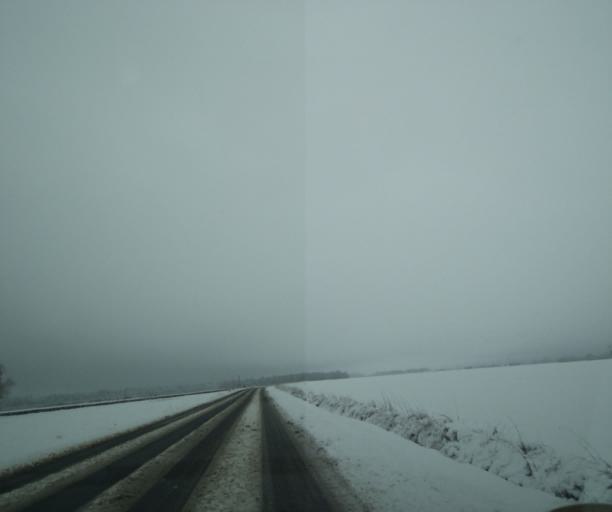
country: FR
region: Champagne-Ardenne
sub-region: Departement de la Haute-Marne
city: Saint-Dizier
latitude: 48.5696
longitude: 4.9184
